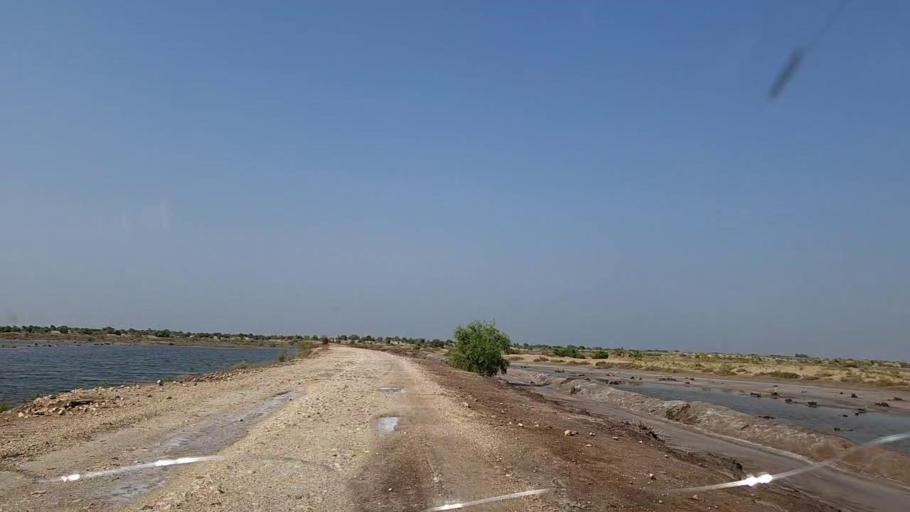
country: PK
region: Sindh
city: Khanpur
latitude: 27.6938
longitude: 69.3837
